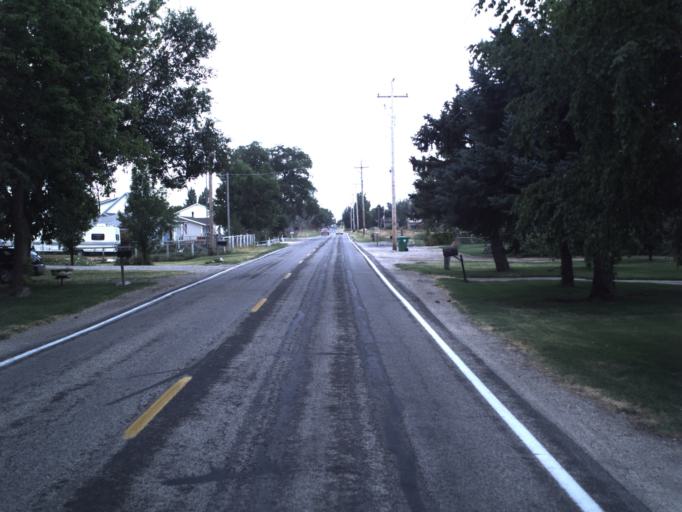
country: US
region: Utah
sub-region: Davis County
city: West Point
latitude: 41.1283
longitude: -112.1126
